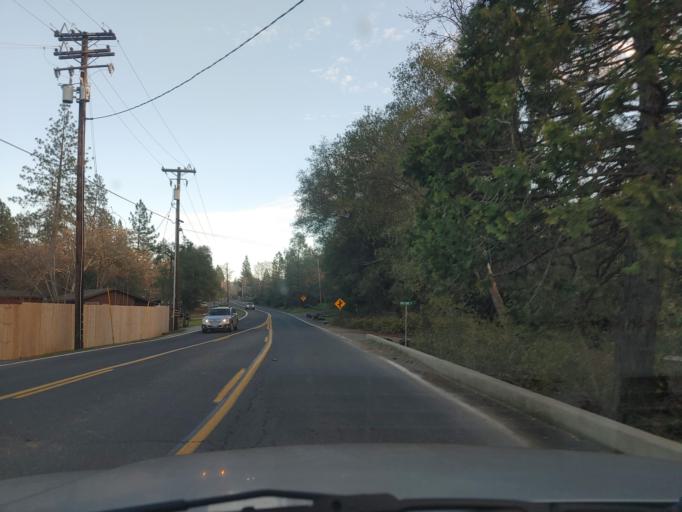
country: US
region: California
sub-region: Tuolumne County
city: Columbia
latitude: 38.0246
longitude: -120.4022
